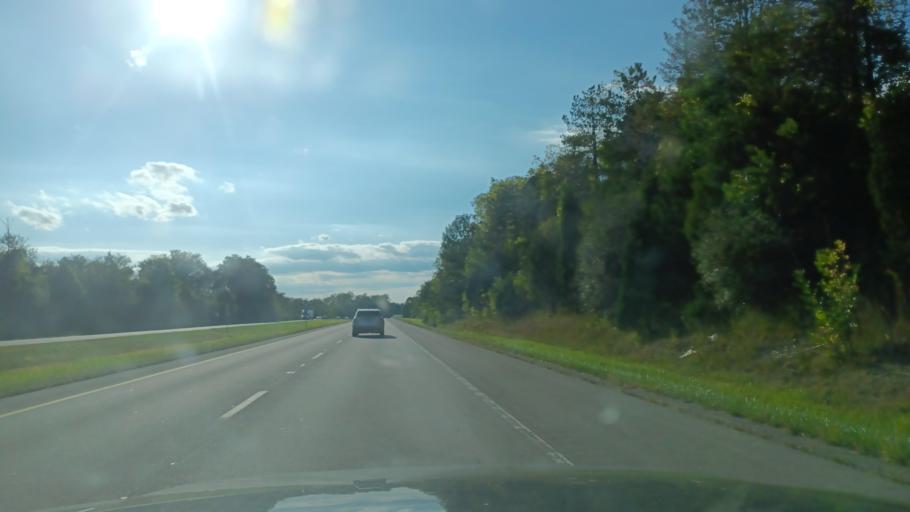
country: US
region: Ohio
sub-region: Greene County
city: Xenia
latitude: 39.6622
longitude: -83.9368
